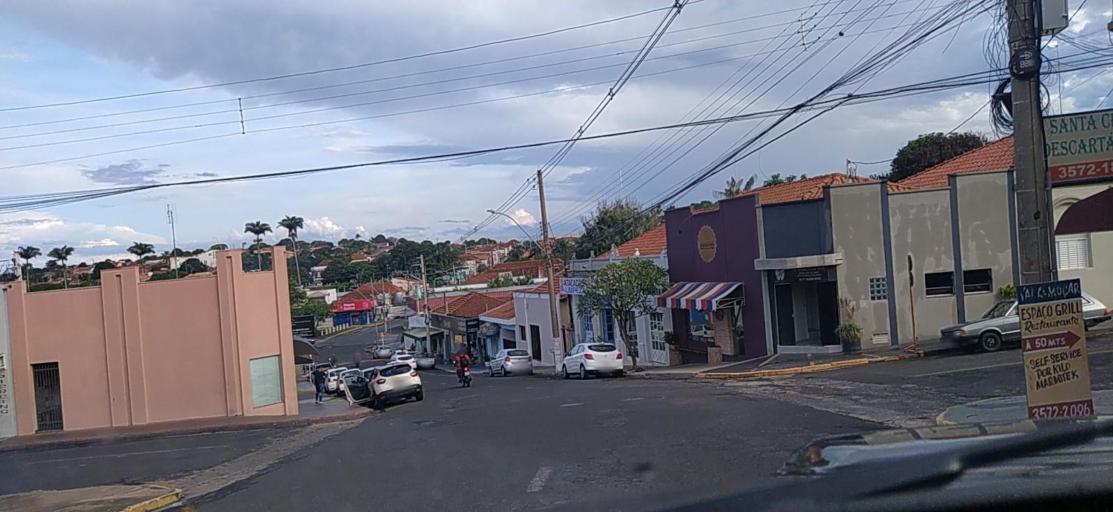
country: BR
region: Sao Paulo
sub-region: Pindorama
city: Pindorama
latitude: -21.1877
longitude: -48.9066
